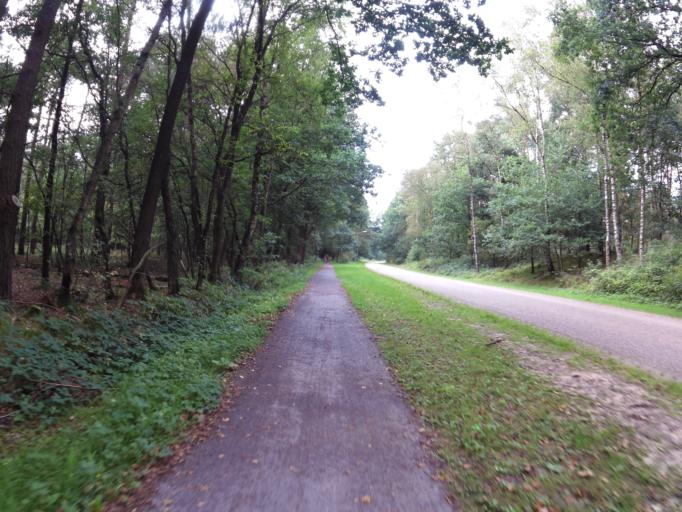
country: NL
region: Drenthe
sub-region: Gemeente Westerveld
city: Dwingeloo
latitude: 52.8139
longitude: 6.3755
